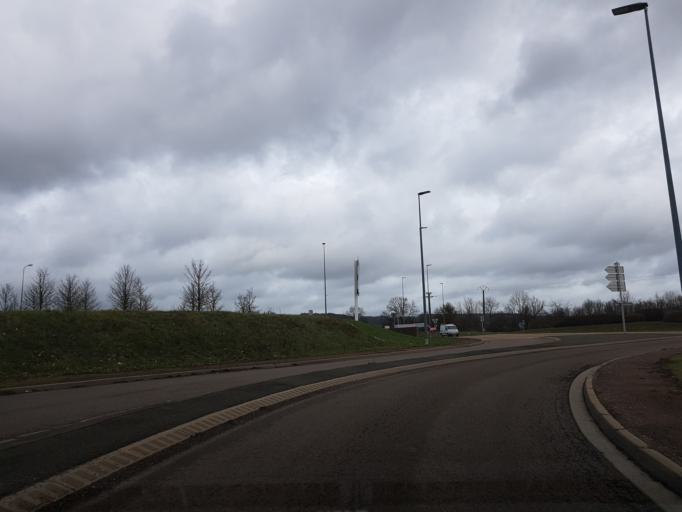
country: FR
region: Champagne-Ardenne
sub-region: Departement de la Haute-Marne
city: Rolampont
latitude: 47.9367
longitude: 5.2883
